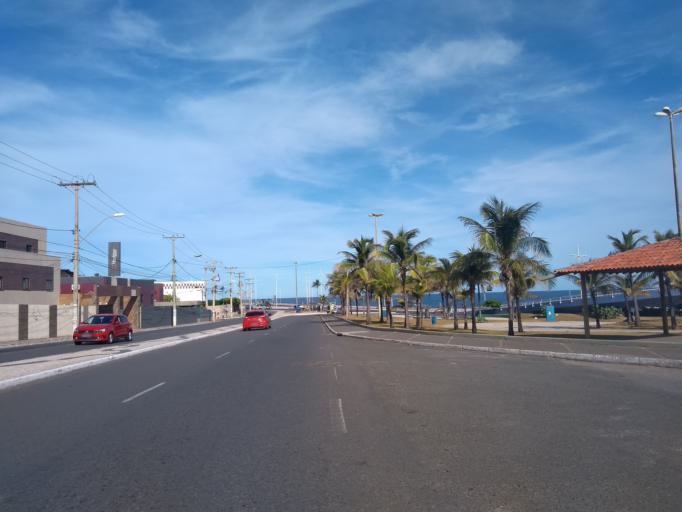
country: BR
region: Bahia
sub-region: Salvador
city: Salvador
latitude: -12.9973
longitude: -38.4463
